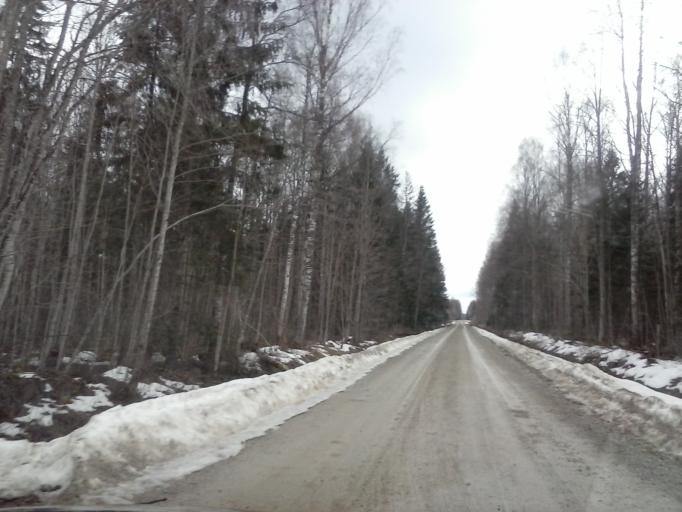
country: EE
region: Jogevamaa
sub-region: Mustvee linn
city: Mustvee
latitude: 59.0752
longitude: 26.8096
